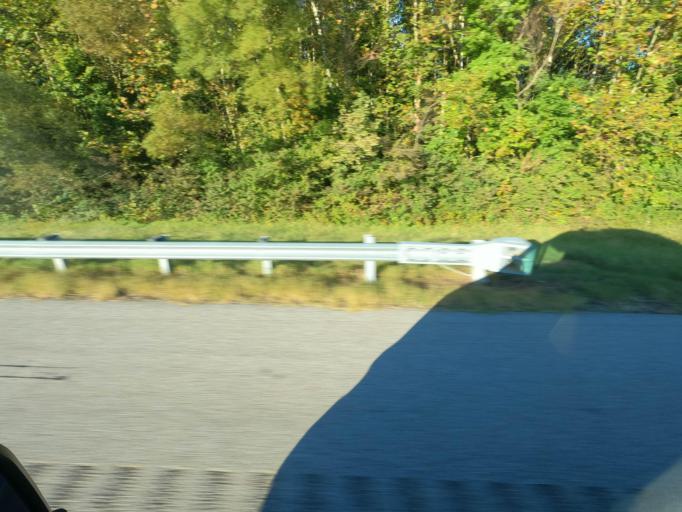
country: US
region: Tennessee
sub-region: Shelby County
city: Millington
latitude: 35.3140
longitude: -89.8642
